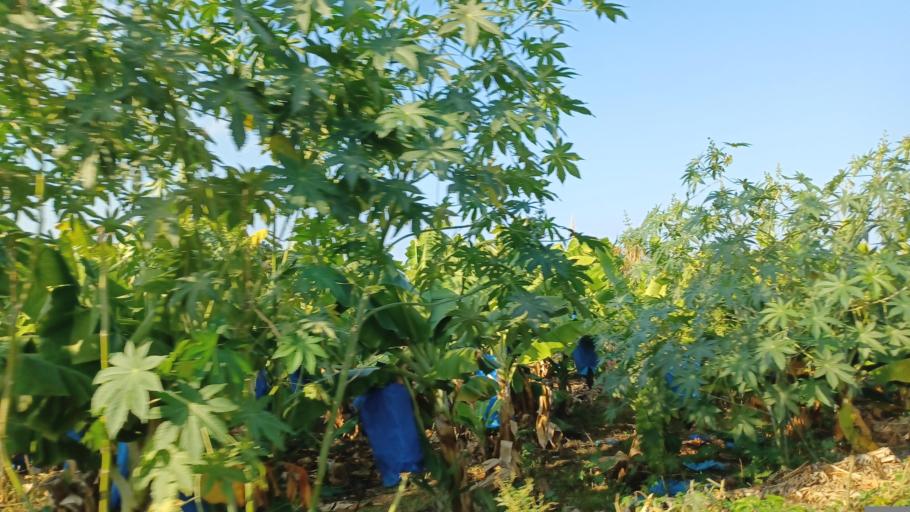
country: CY
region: Pafos
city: Kissonerga
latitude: 34.8230
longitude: 32.3985
